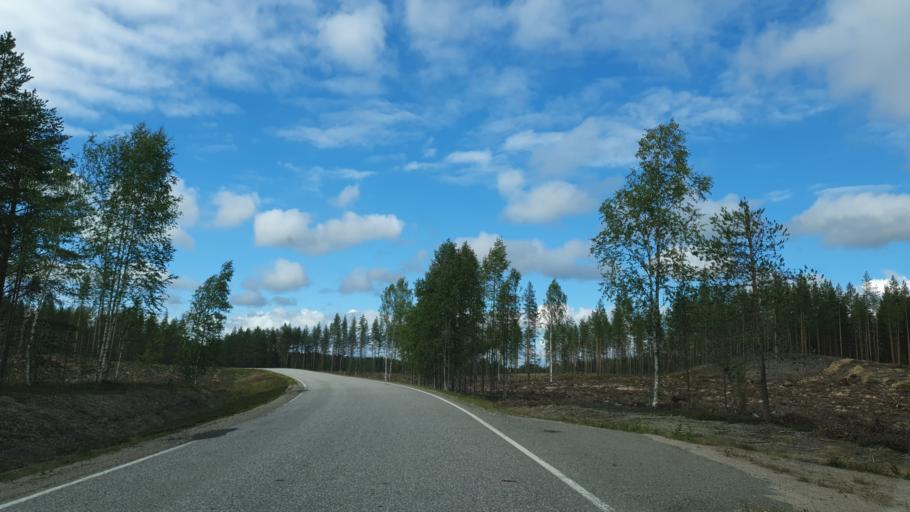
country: FI
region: Kainuu
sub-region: Kehys-Kainuu
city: Kuhmo
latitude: 64.2059
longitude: 29.1803
